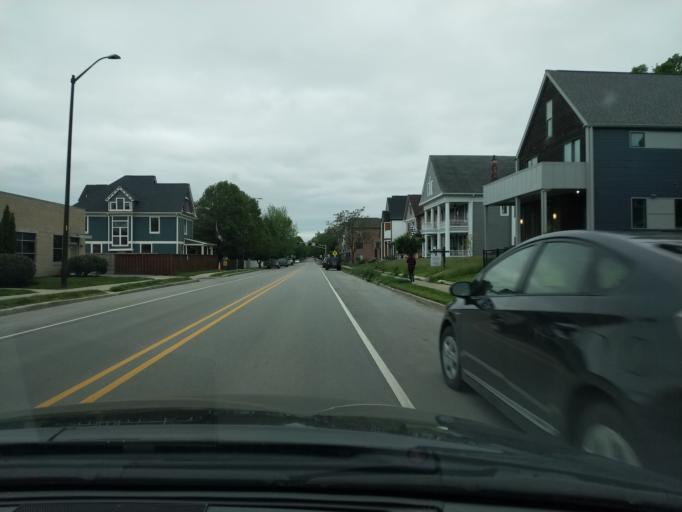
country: US
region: Indiana
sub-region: Marion County
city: Indianapolis
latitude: 39.7938
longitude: -86.1495
